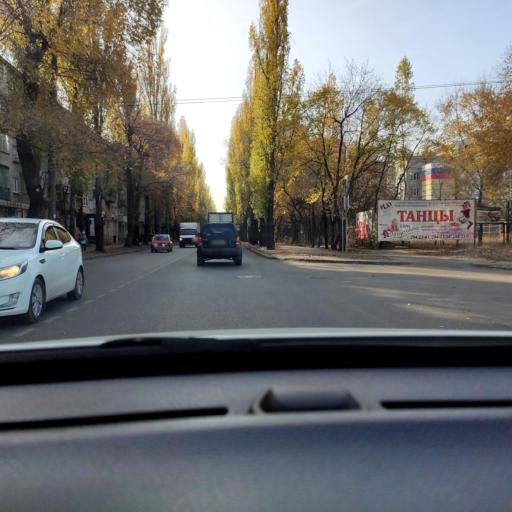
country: RU
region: Voronezj
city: Voronezh
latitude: 51.6858
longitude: 39.2576
